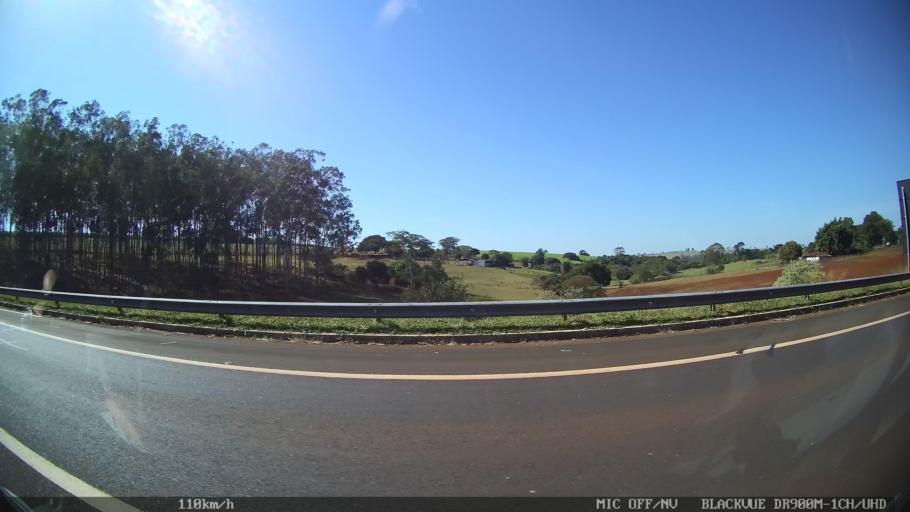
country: BR
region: Sao Paulo
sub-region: Batatais
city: Batatais
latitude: -20.8449
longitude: -47.6012
